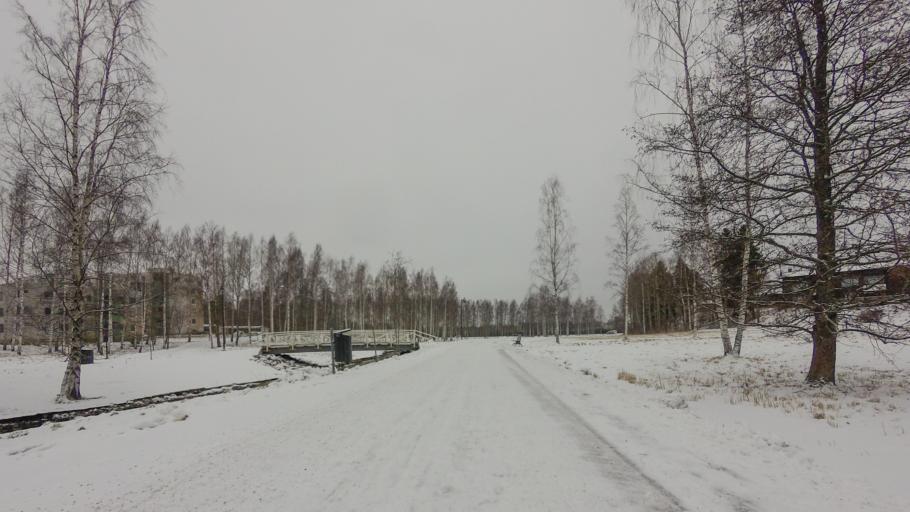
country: FI
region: Uusimaa
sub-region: Helsinki
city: Vantaa
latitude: 60.2003
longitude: 25.0695
